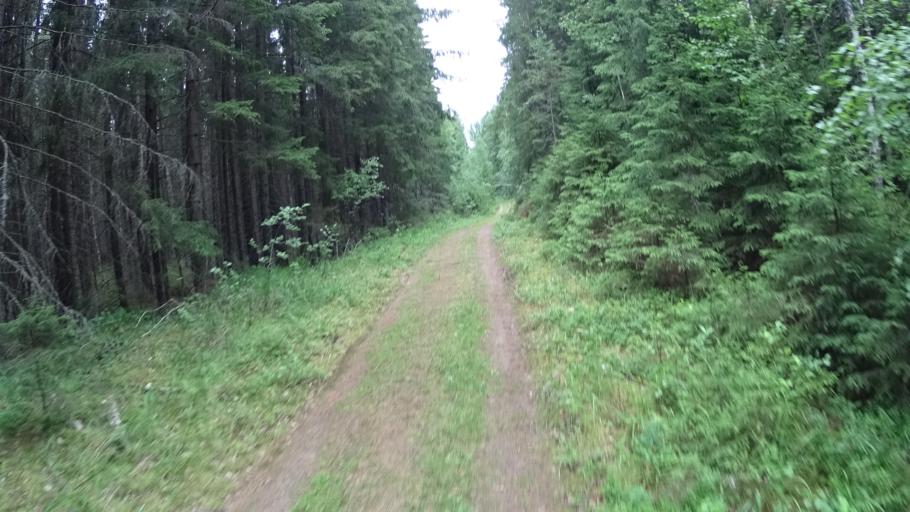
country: FI
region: Southern Savonia
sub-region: Mikkeli
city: Maentyharju
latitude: 61.1850
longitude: 26.8294
